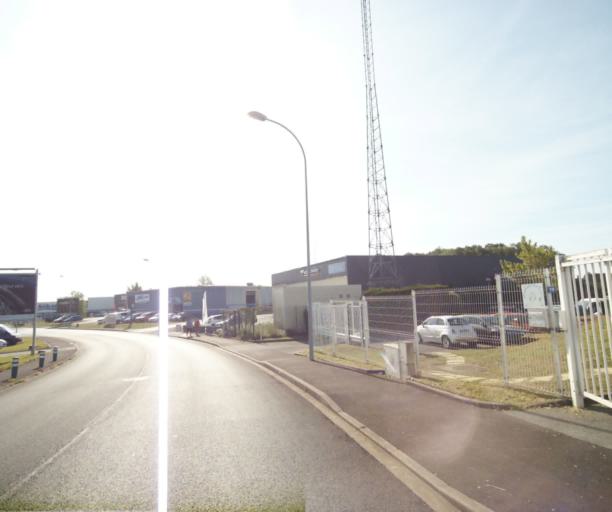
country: FR
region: Champagne-Ardenne
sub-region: Departement des Ardennes
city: La Francheville
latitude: 49.7376
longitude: 4.7014
